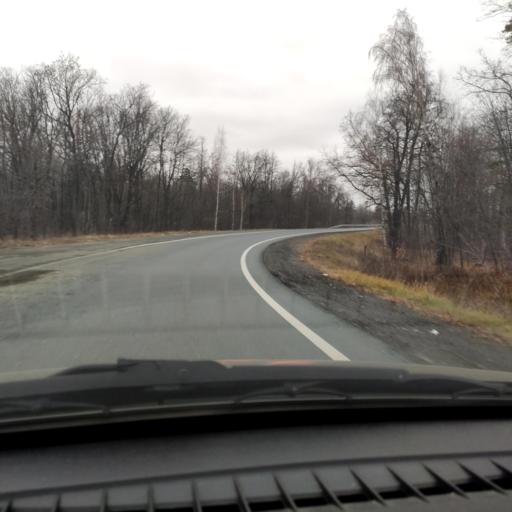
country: RU
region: Samara
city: Pribrezhnyy
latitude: 53.5099
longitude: 49.9308
